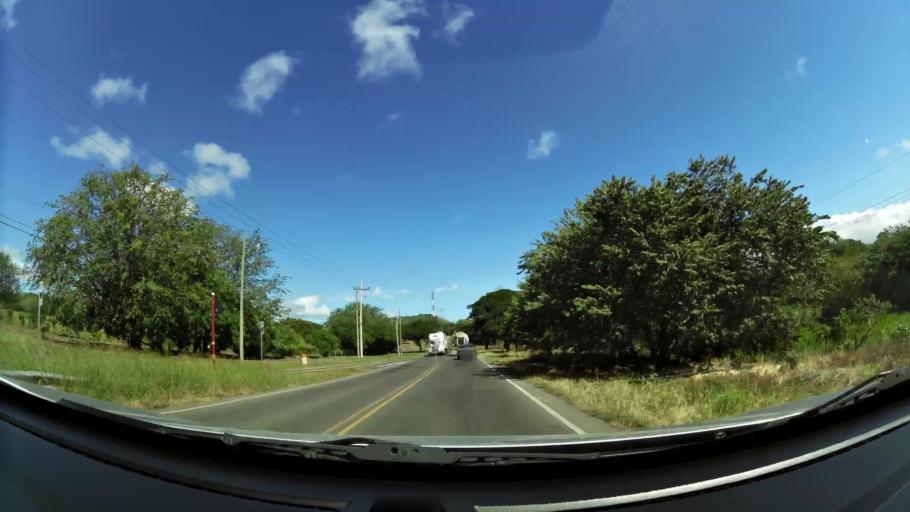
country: CR
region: Guanacaste
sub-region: Canton de Canas
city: Canas
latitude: 10.3909
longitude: -85.0809
